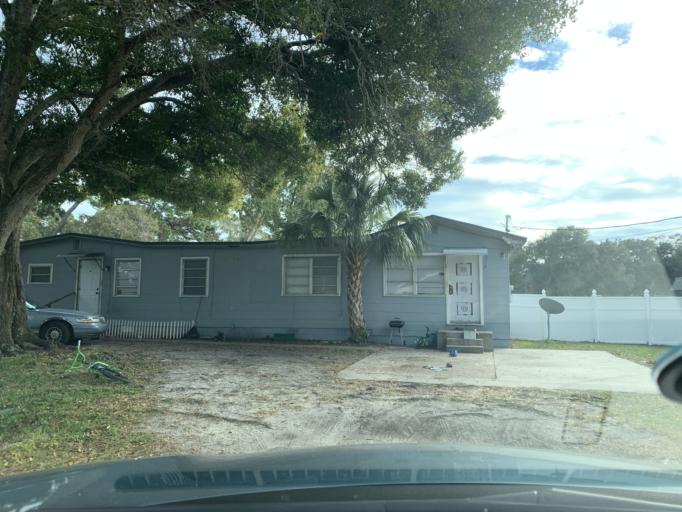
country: US
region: Florida
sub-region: Pinellas County
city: Kenneth City
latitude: 27.8201
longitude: -82.7350
